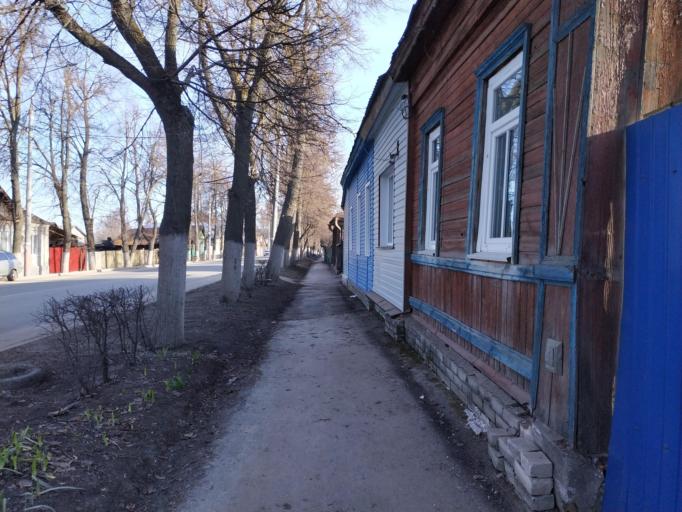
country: RU
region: Nizjnij Novgorod
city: Arzamas
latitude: 55.3931
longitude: 43.8121
